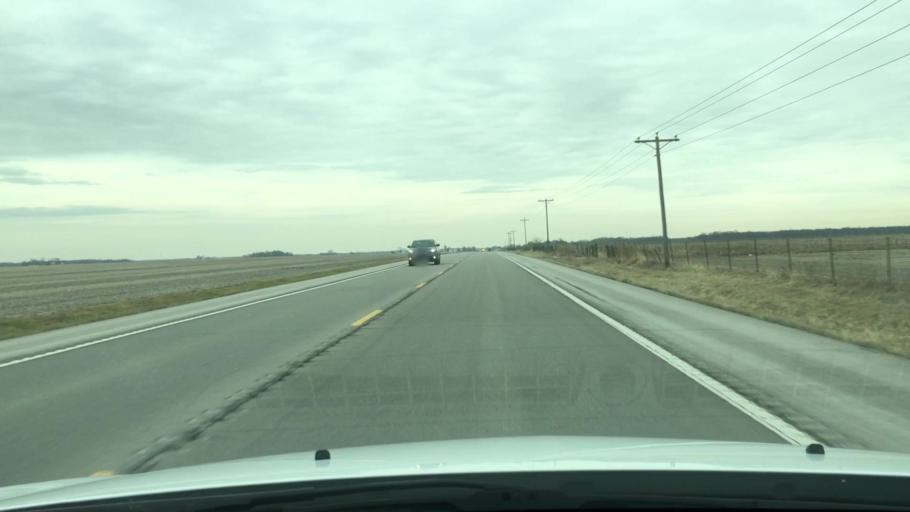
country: US
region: Missouri
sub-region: Audrain County
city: Mexico
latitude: 39.1640
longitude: -91.7337
